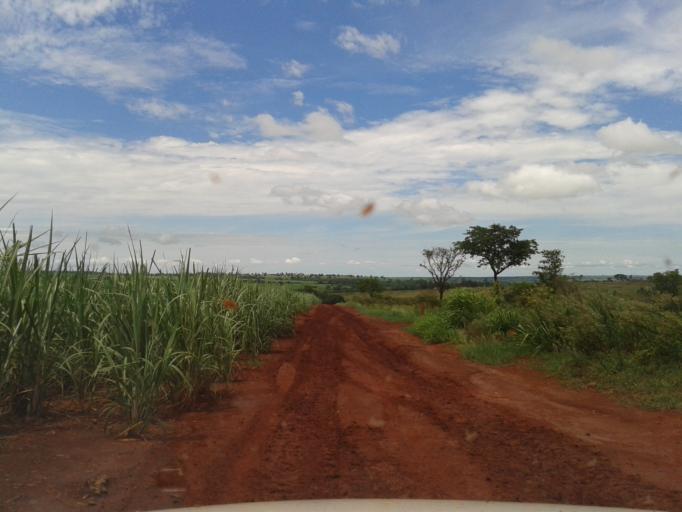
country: BR
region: Minas Gerais
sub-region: Santa Vitoria
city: Santa Vitoria
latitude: -19.2152
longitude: -50.6593
